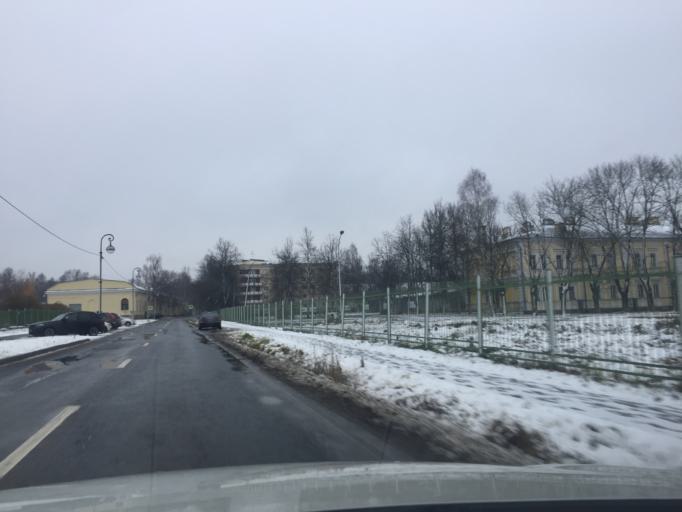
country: RU
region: St.-Petersburg
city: Pushkin
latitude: 59.7051
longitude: 30.3960
